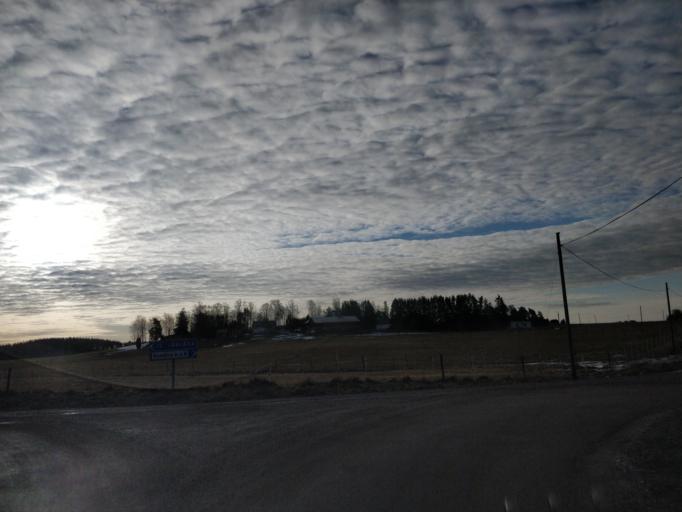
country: SE
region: Uppsala
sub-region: Enkopings Kommun
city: Enkoping
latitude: 59.8139
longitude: 17.1172
